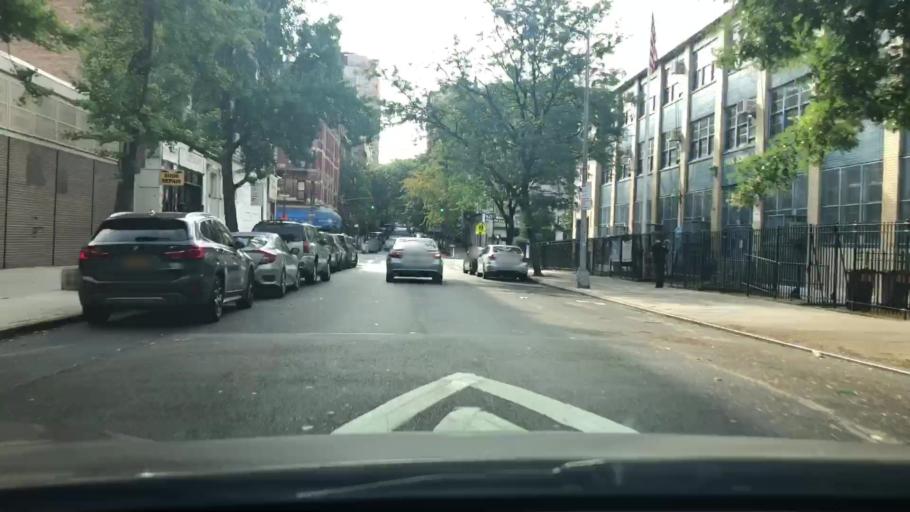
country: US
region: New York
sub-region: New York County
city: Manhattan
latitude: 40.7855
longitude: -73.9740
